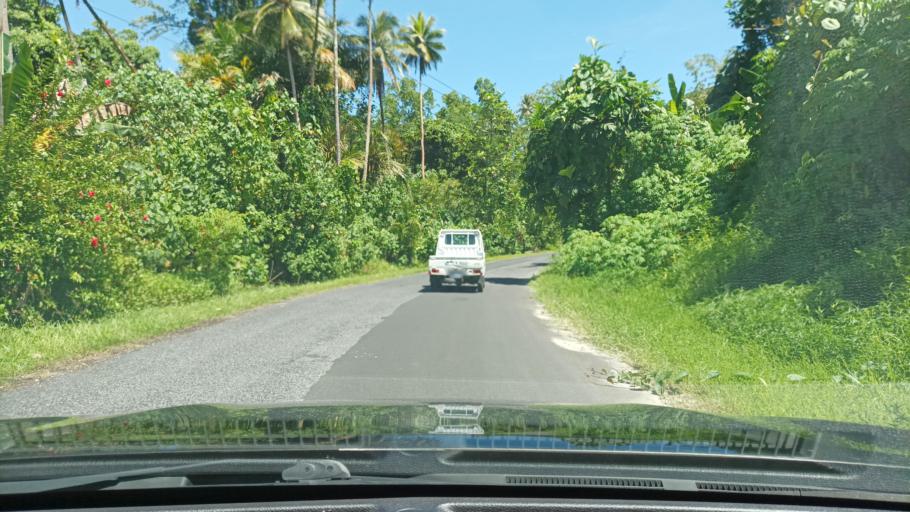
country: FM
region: Pohnpei
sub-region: Madolenihm Municipality
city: Madolenihm Municipality Government
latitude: 6.9158
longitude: 158.3209
